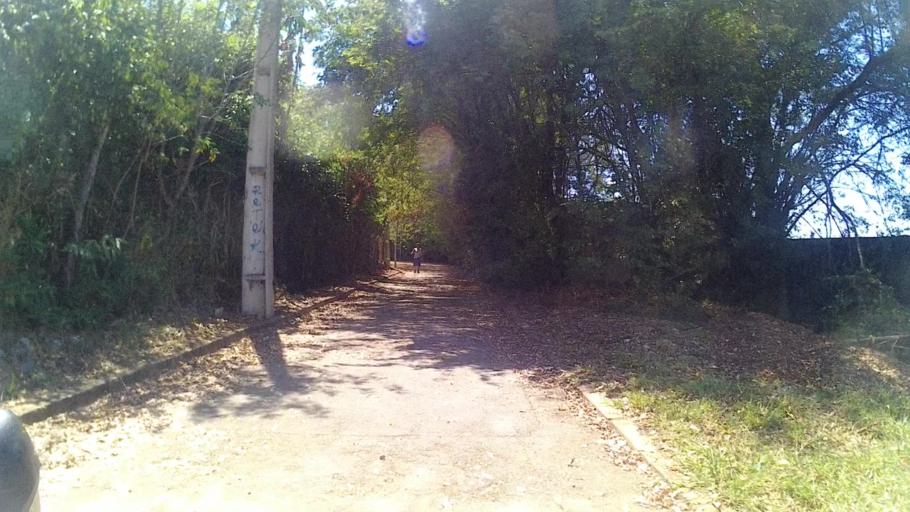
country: BR
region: Federal District
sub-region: Brasilia
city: Brasilia
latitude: -15.7298
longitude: -47.8806
